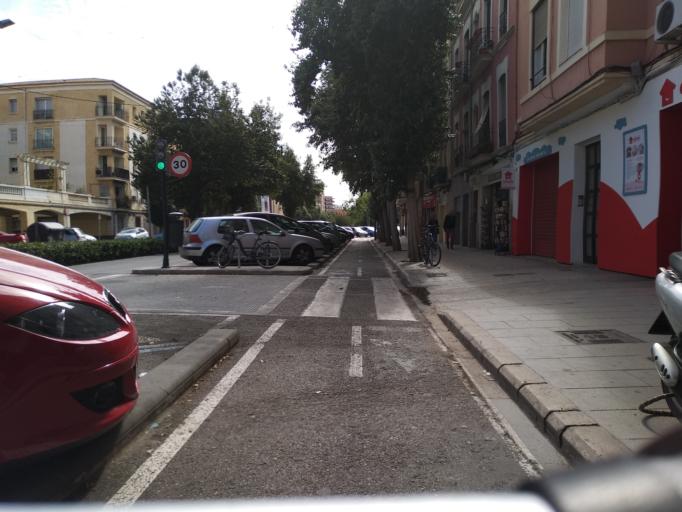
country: ES
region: Valencia
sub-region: Provincia de Valencia
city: Tavernes Blanques
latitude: 39.4848
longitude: -0.3688
